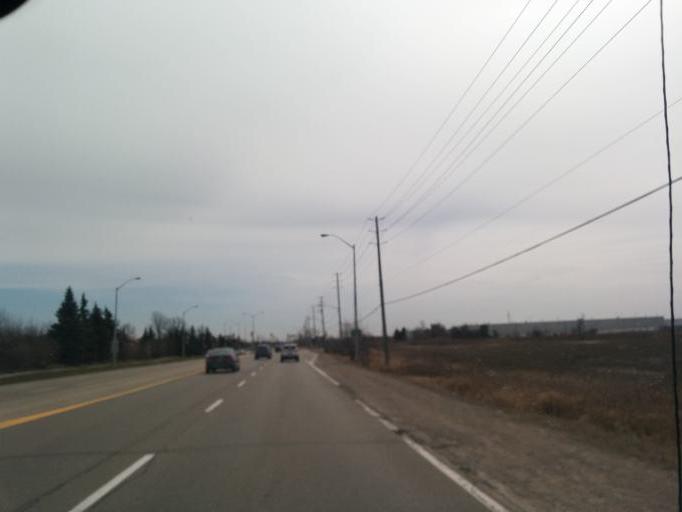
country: CA
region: Ontario
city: Brampton
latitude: 43.7233
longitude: -79.8107
